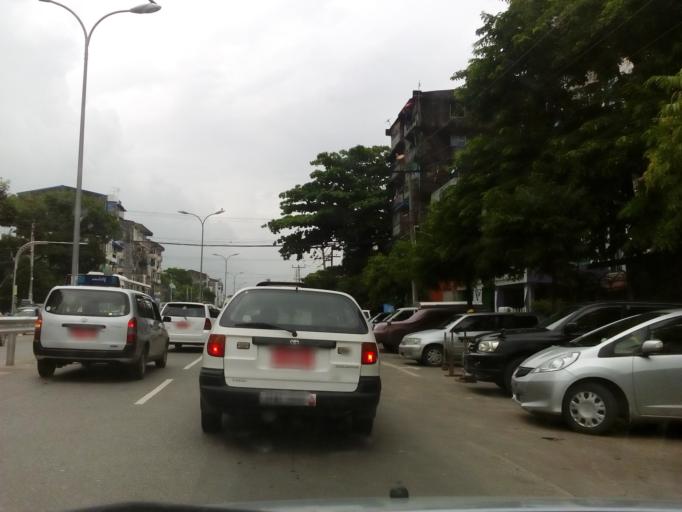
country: MM
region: Yangon
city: Yangon
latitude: 16.8140
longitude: 96.1696
